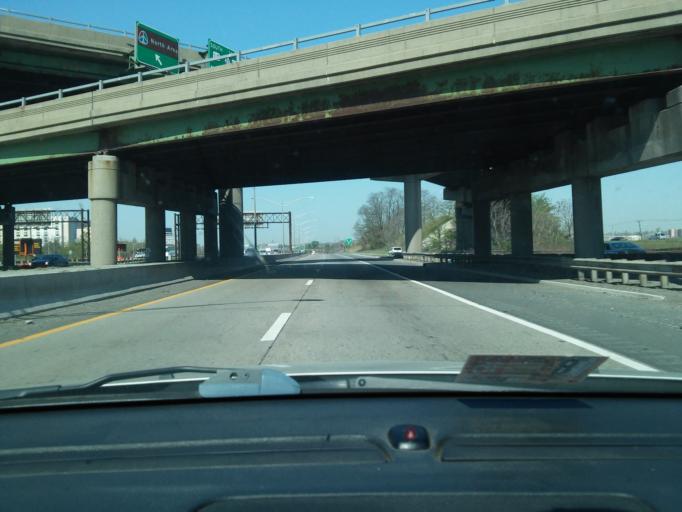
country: US
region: New Jersey
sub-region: Essex County
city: Newark
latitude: 40.7108
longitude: -74.1661
